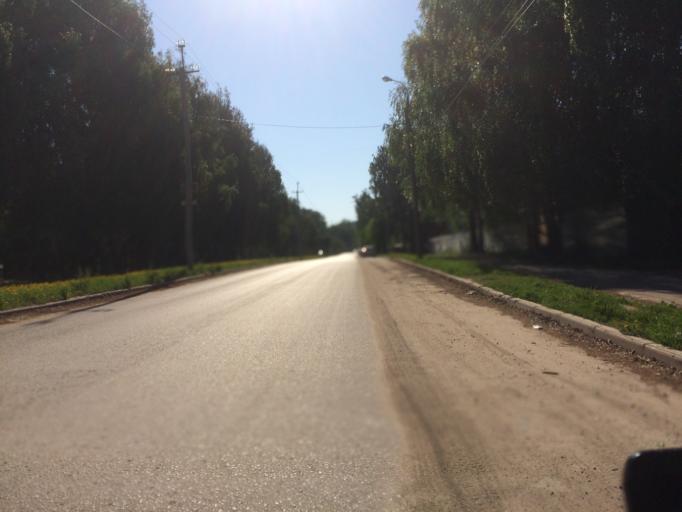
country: RU
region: Mariy-El
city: Medvedevo
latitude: 56.6472
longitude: 47.8457
